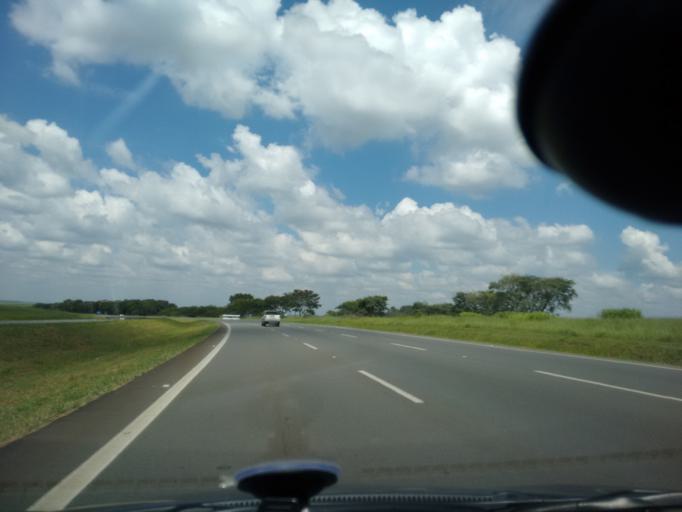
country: BR
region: Sao Paulo
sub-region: Santa Barbara D'Oeste
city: Santa Barbara d'Oeste
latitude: -22.7744
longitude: -47.4449
